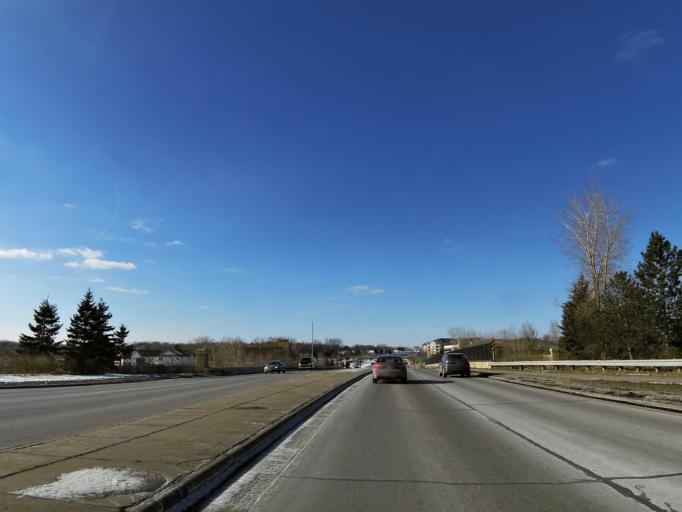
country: US
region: Minnesota
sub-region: Washington County
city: Woodbury
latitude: 44.9154
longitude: -92.9784
